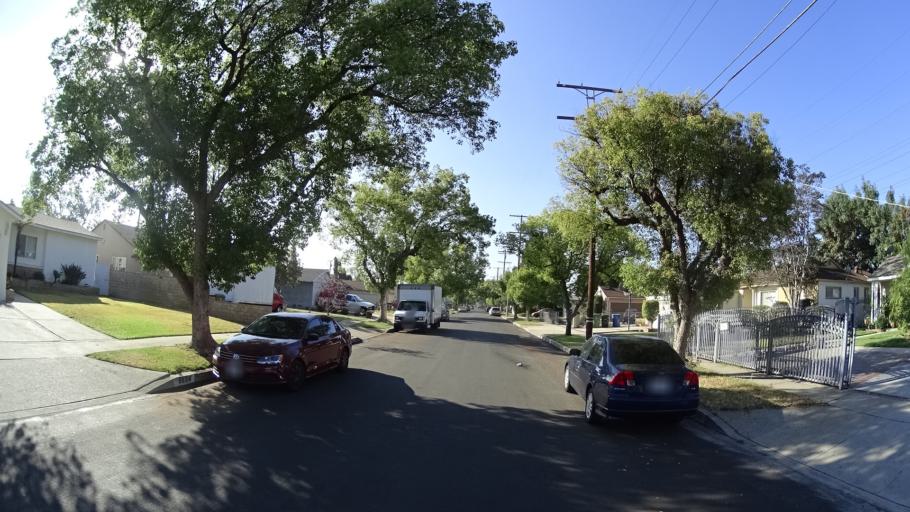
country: US
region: California
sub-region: Los Angeles County
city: Van Nuys
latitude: 34.2306
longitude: -118.4242
